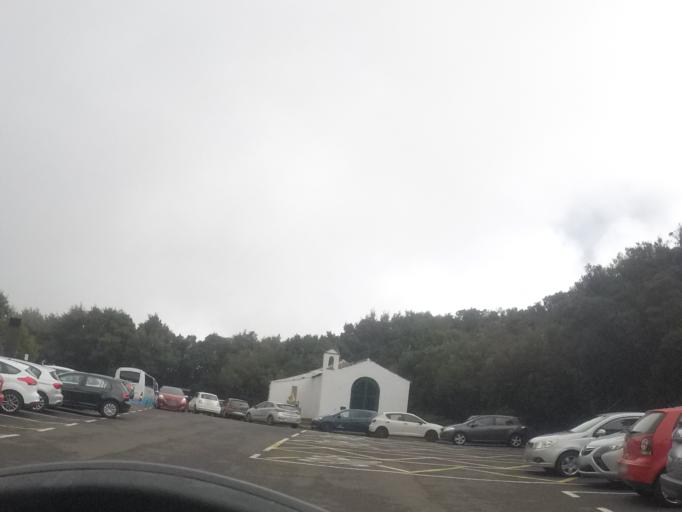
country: ES
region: Canary Islands
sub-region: Provincia de Santa Cruz de Tenerife
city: Tegueste
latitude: 28.5308
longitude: -16.2799
